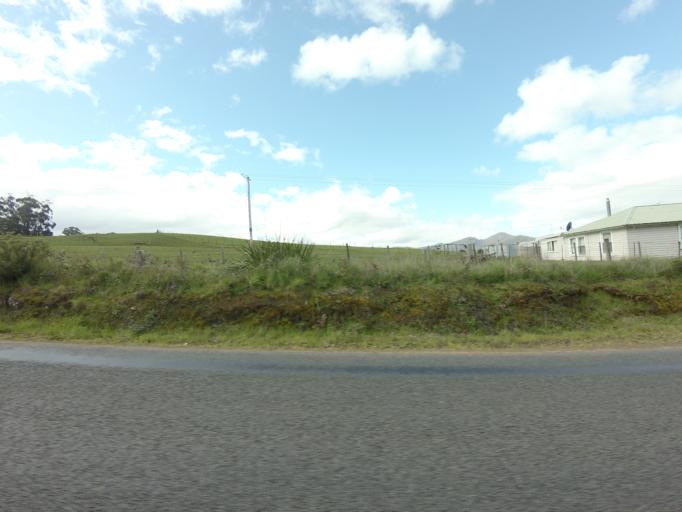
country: AU
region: Tasmania
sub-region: Huon Valley
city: Geeveston
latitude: -43.2020
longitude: 146.9644
